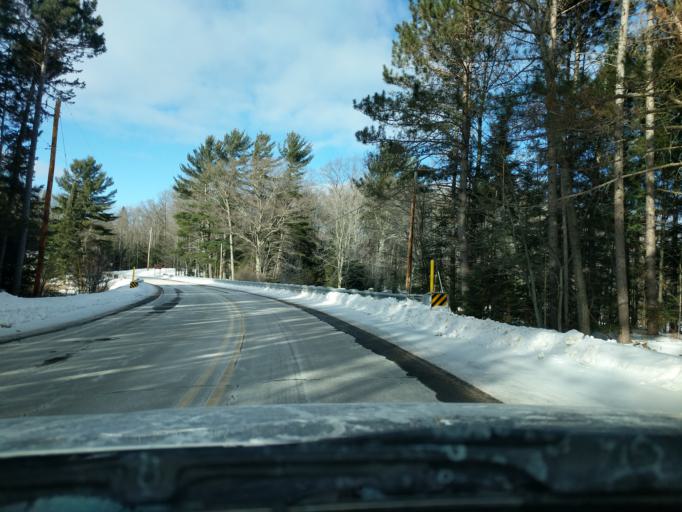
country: US
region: Wisconsin
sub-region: Vilas County
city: Eagle River
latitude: 45.7804
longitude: -89.0740
